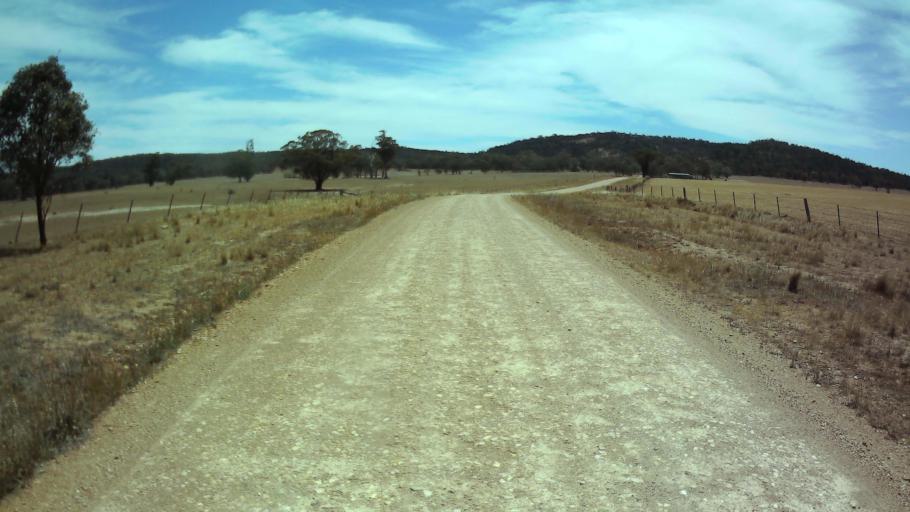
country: AU
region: New South Wales
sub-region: Weddin
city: Grenfell
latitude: -33.7493
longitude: 148.2057
